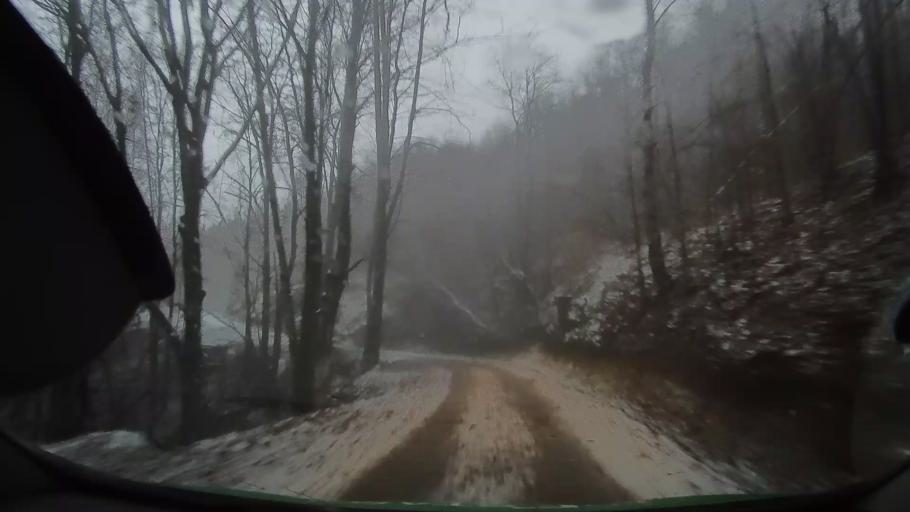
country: RO
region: Alba
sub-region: Comuna Avram Iancu
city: Avram Iancu
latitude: 46.3007
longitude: 22.7931
